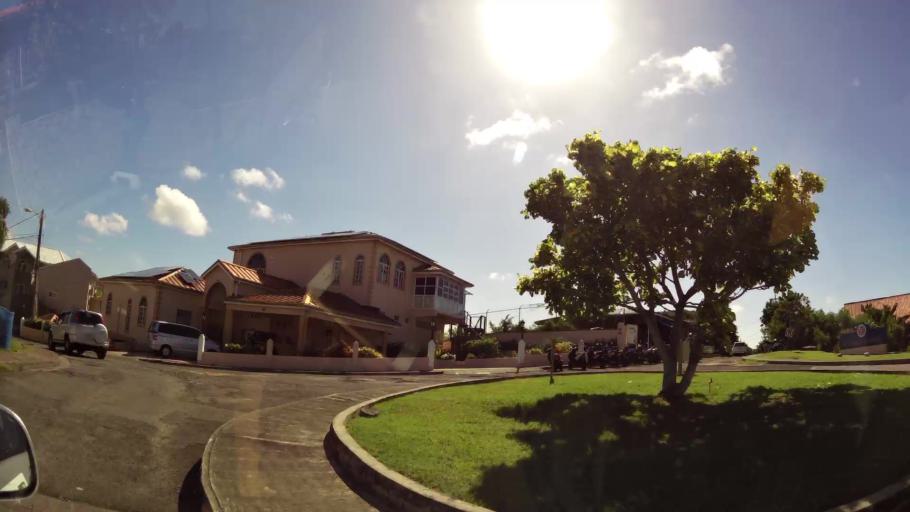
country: GD
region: Saint George
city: Saint George's
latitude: 12.0016
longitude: -61.7721
